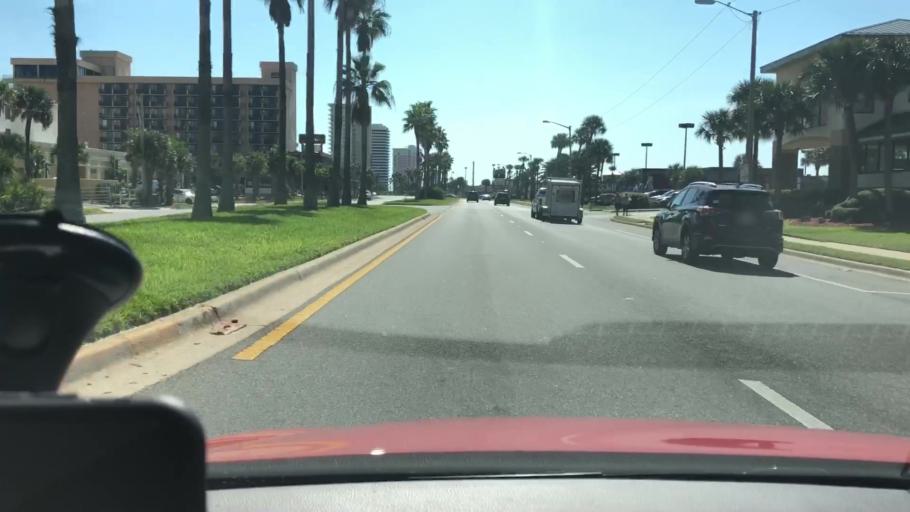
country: US
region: Florida
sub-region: Volusia County
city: Holly Hill
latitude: 29.2644
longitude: -81.0268
